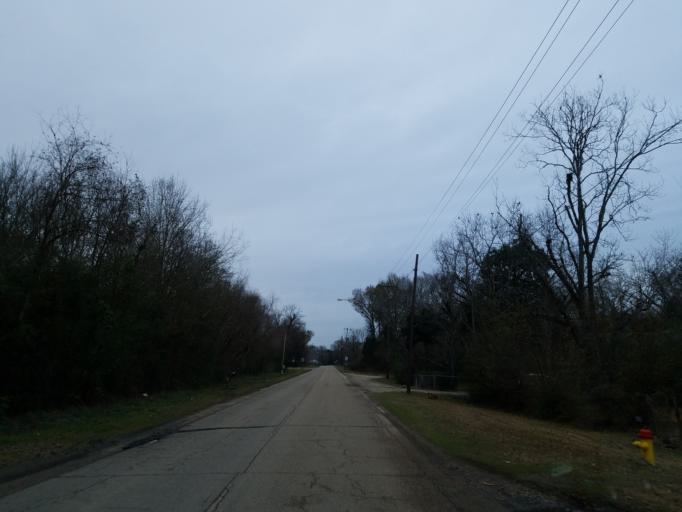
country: US
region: Mississippi
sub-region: Forrest County
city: Hattiesburg
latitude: 31.2958
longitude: -89.2713
